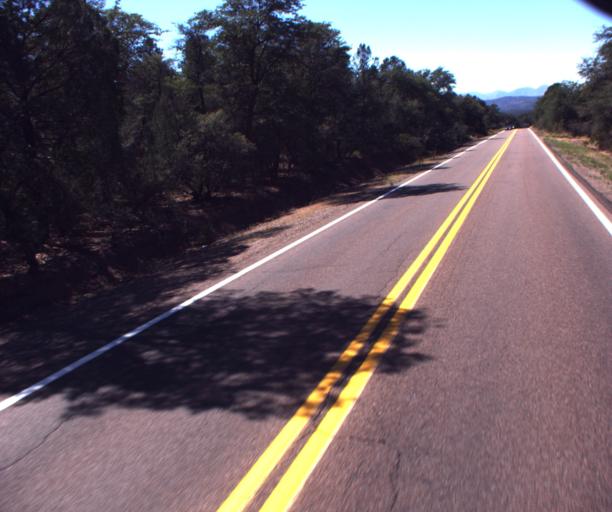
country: US
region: Arizona
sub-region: Gila County
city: Star Valley
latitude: 34.2636
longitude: -111.1993
